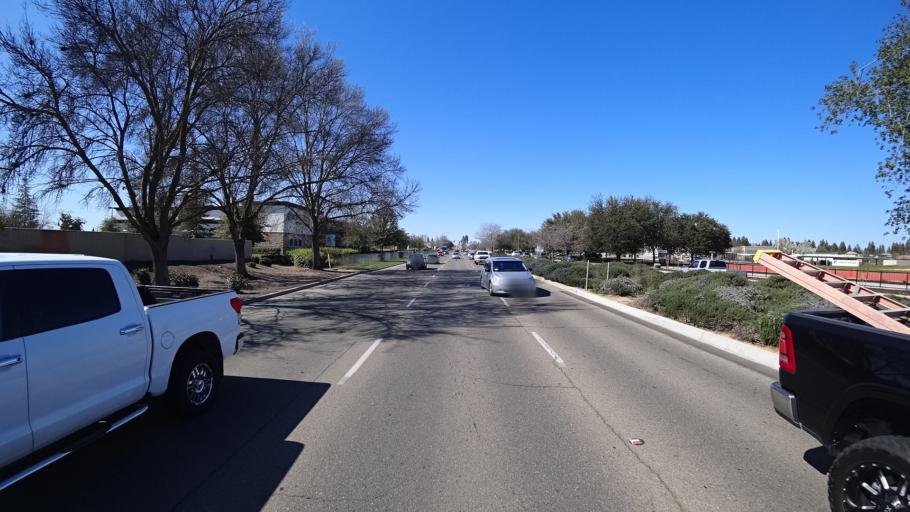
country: US
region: California
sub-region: Fresno County
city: West Park
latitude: 36.8370
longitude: -119.8763
